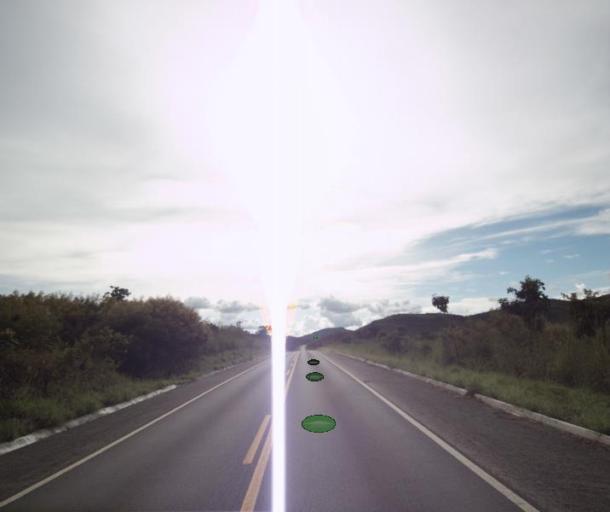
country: BR
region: Goias
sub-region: Barro Alto
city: Barro Alto
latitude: -15.1176
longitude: -48.7351
